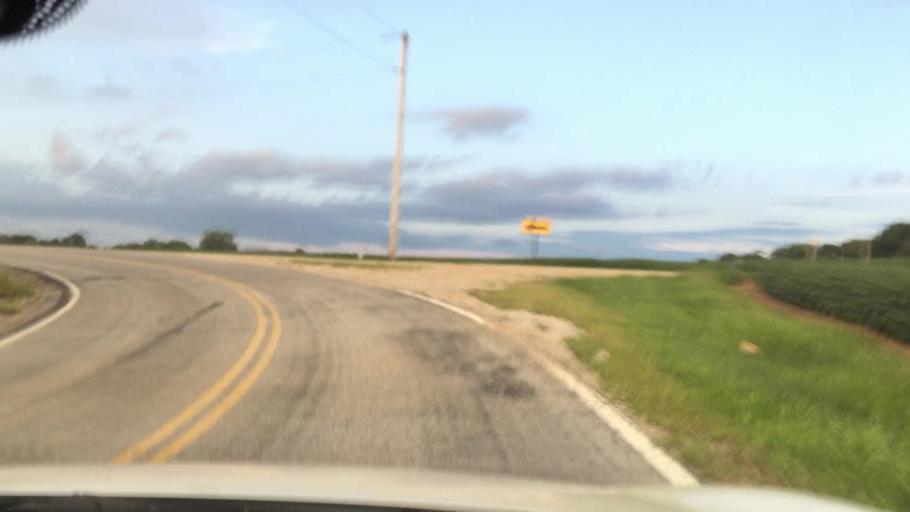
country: US
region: Ohio
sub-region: Champaign County
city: Mechanicsburg
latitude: 39.9948
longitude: -83.6380
